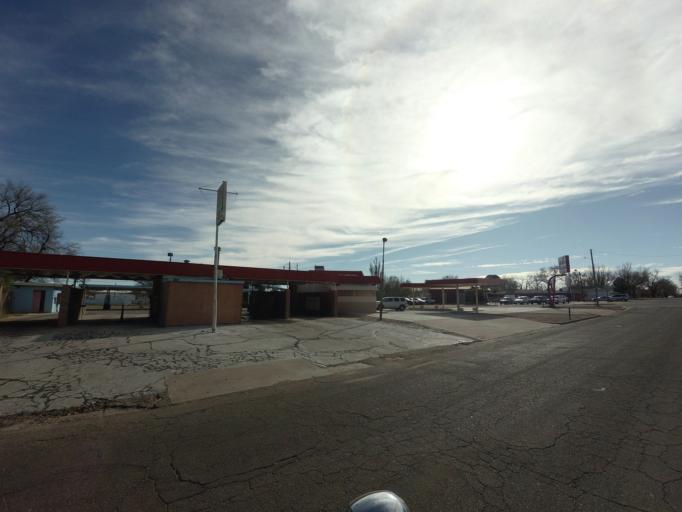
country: US
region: New Mexico
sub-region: Curry County
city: Clovis
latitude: 34.4152
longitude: -103.2029
